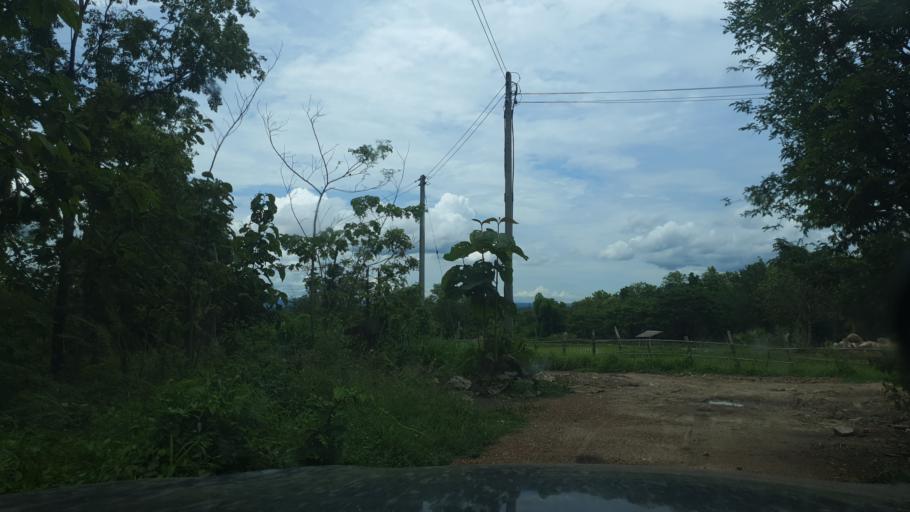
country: TH
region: Lampang
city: Sop Prap
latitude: 17.8568
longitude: 99.3960
